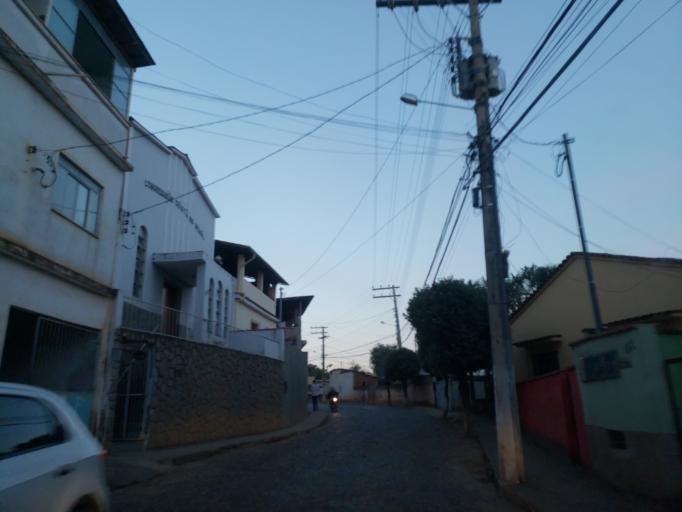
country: BR
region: Minas Gerais
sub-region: Sao Joao Nepomuceno
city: Sao Joao Nepomuceno
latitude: -21.5242
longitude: -43.0149
